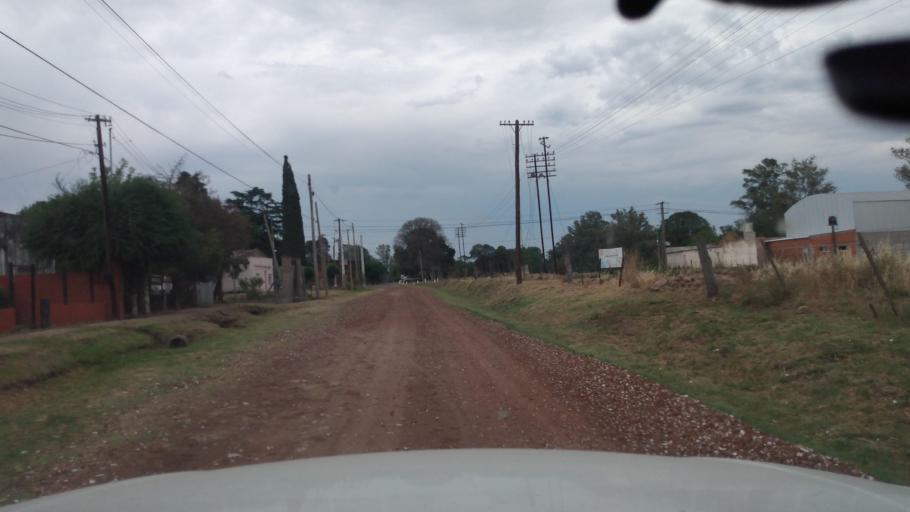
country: AR
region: Buenos Aires
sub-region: Partido de Lujan
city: Lujan
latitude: -34.5544
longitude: -59.2040
